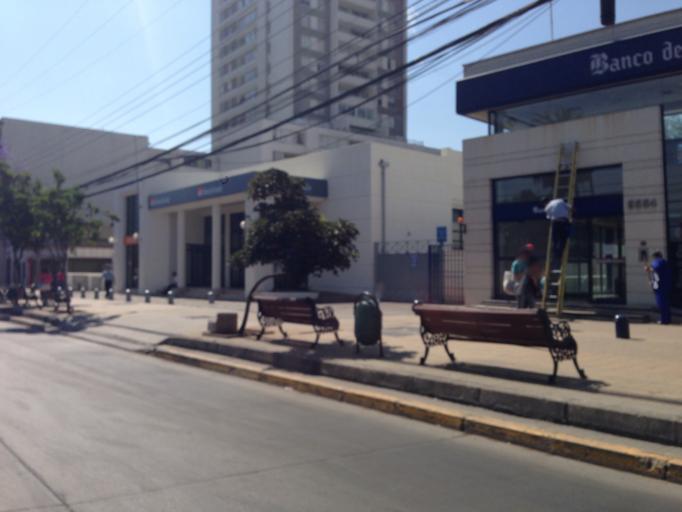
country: CL
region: Santiago Metropolitan
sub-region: Provincia de Santiago
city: Villa Presidente Frei, Nunoa, Santiago, Chile
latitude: -33.4534
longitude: -70.5725
